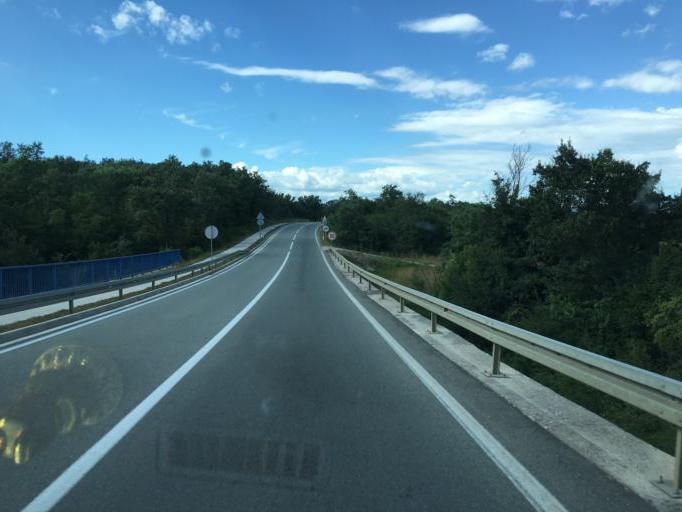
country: HR
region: Primorsko-Goranska
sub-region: Grad Krk
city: Krk
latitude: 45.0592
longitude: 14.5561
